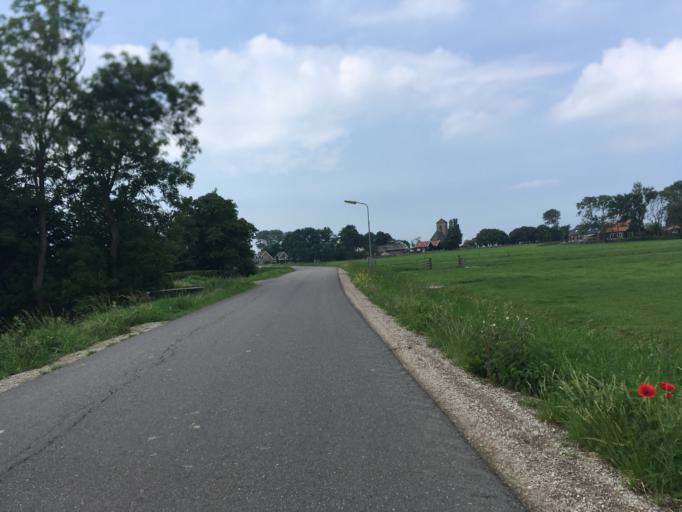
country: NL
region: North Holland
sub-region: Gemeente Haarlem
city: Haarlem
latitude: 52.4055
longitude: 4.6991
